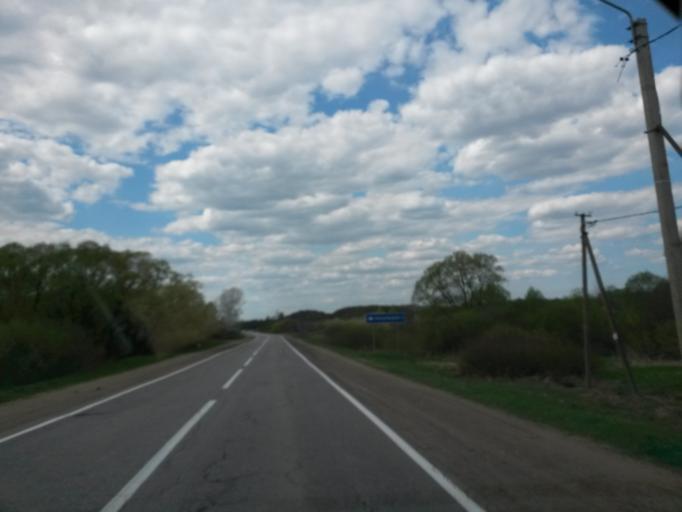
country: RU
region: Jaroslavl
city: Kurba
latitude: 57.6789
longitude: 39.5709
